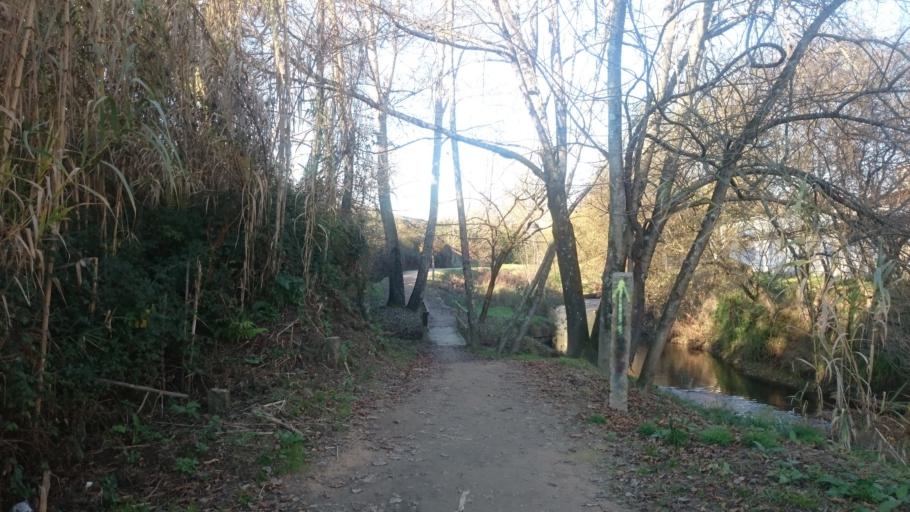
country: ES
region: Galicia
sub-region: Provincia de Pontevedra
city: Porrino
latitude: 42.1606
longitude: -8.6249
